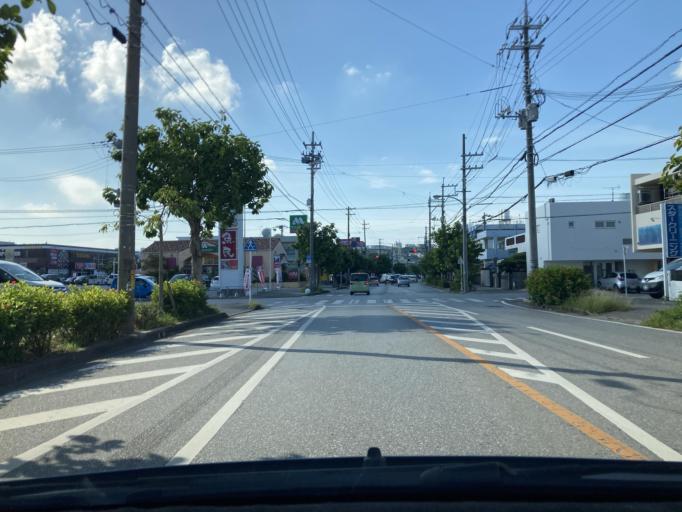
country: JP
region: Okinawa
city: Okinawa
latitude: 26.3214
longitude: 127.8317
